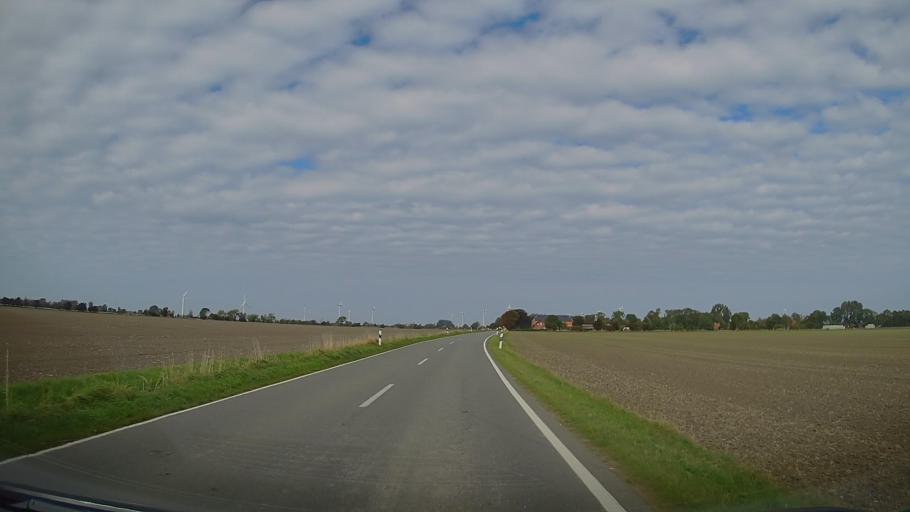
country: DE
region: Schleswig-Holstein
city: Grossenbrode
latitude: 54.4911
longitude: 11.0614
